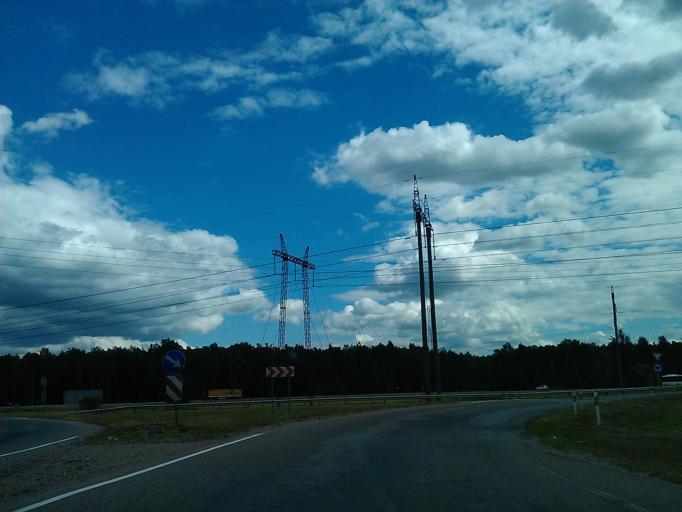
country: LV
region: Jelgava
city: Jelgava
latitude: 56.6299
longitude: 23.7496
